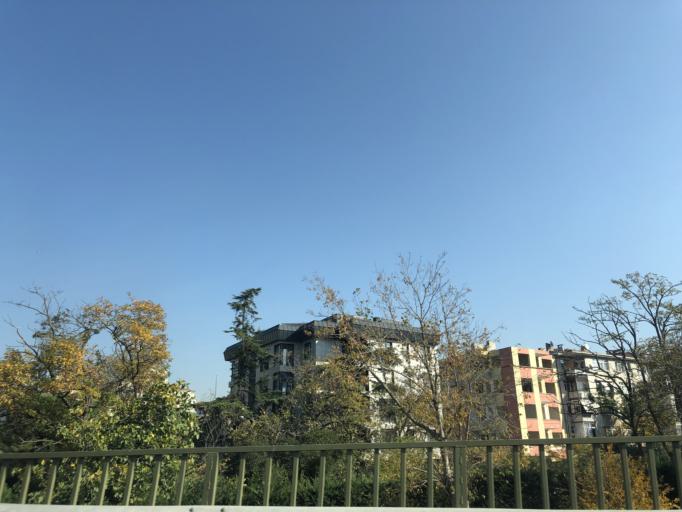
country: TR
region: Istanbul
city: UEskuedar
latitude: 40.9970
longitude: 29.0313
